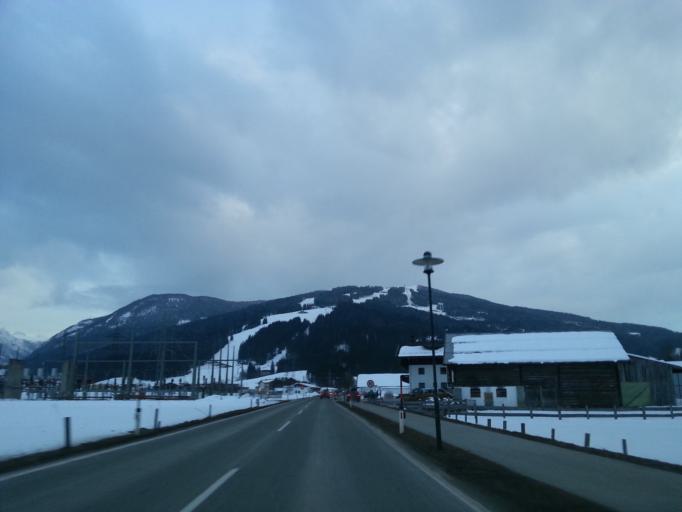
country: AT
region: Salzburg
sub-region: Politischer Bezirk Sankt Johann im Pongau
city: Flachau
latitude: 47.3661
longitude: 13.3848
